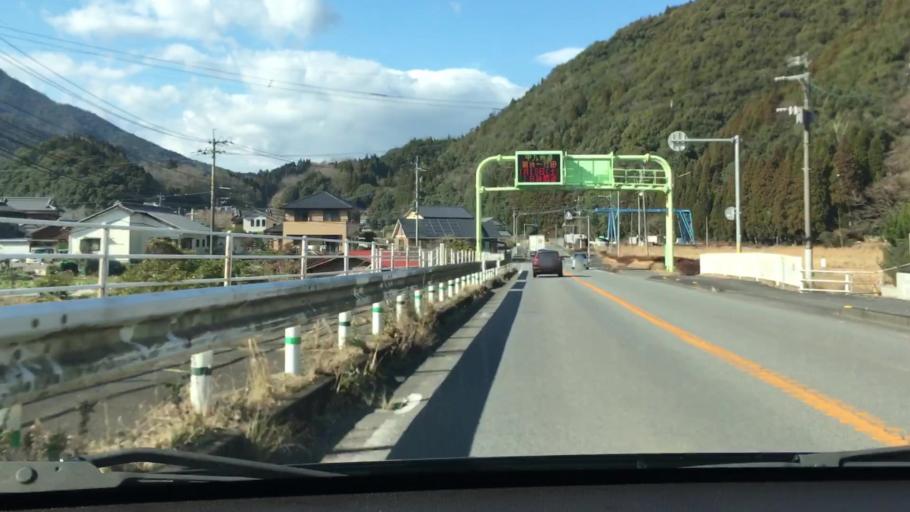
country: JP
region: Oita
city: Saiki
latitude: 32.9871
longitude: 131.8384
